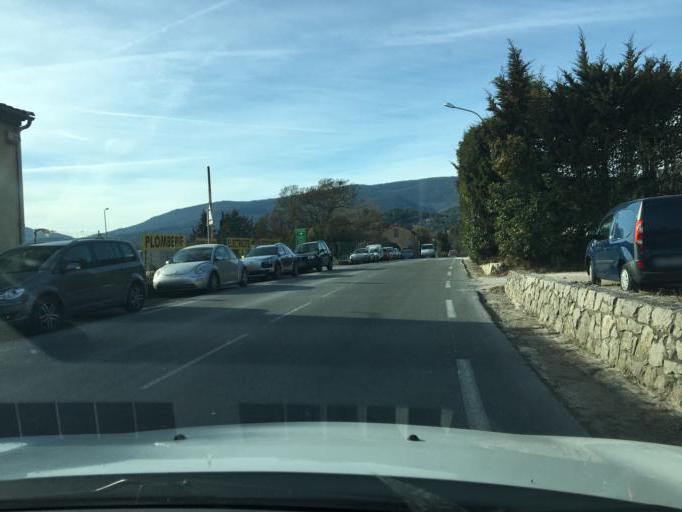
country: FR
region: Provence-Alpes-Cote d'Azur
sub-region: Departement du Var
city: Fayence
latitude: 43.6221
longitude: 6.6899
